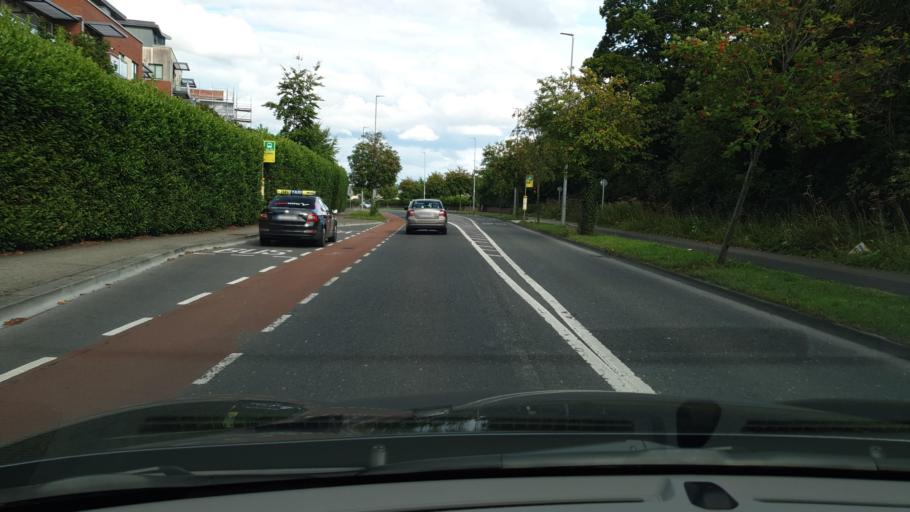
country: IE
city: Palmerstown
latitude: 53.3541
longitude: -6.4084
